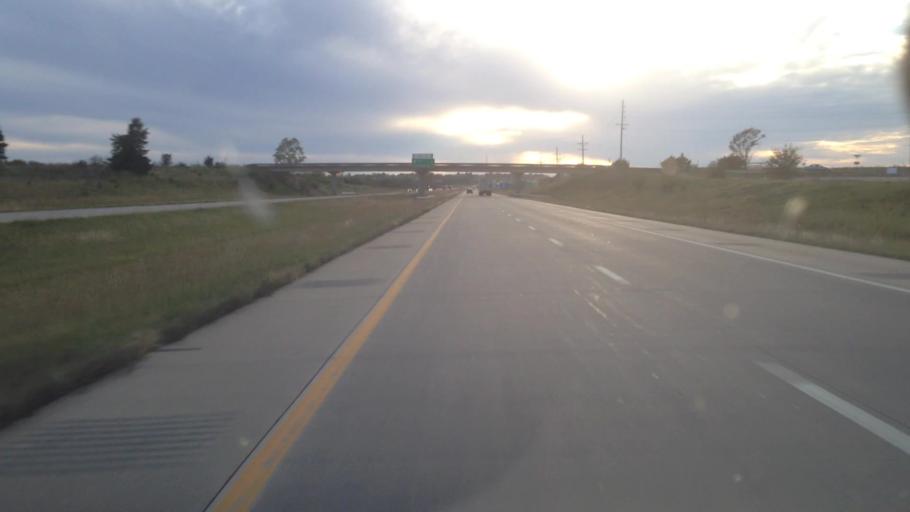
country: US
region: Kansas
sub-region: Franklin County
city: Ottawa
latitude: 38.5828
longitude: -95.2471
